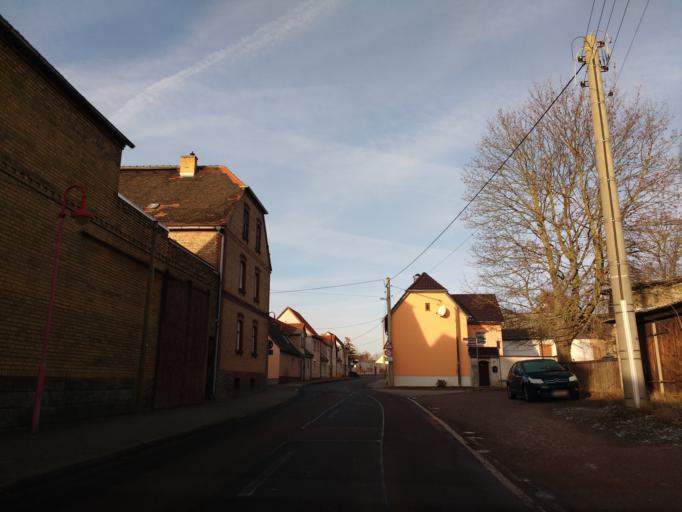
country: DE
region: Saxony-Anhalt
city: Oppin
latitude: 51.5511
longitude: 12.0349
